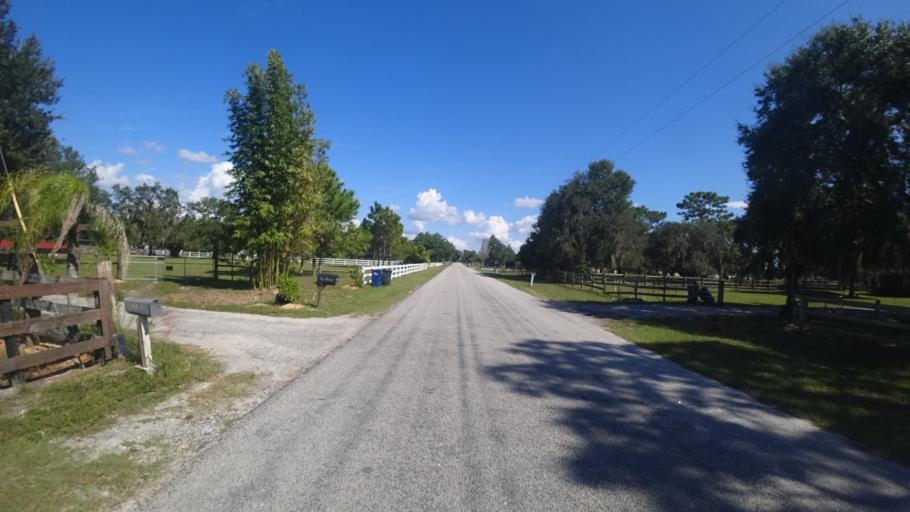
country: US
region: Florida
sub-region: Sarasota County
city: The Meadows
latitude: 27.4671
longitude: -82.2937
